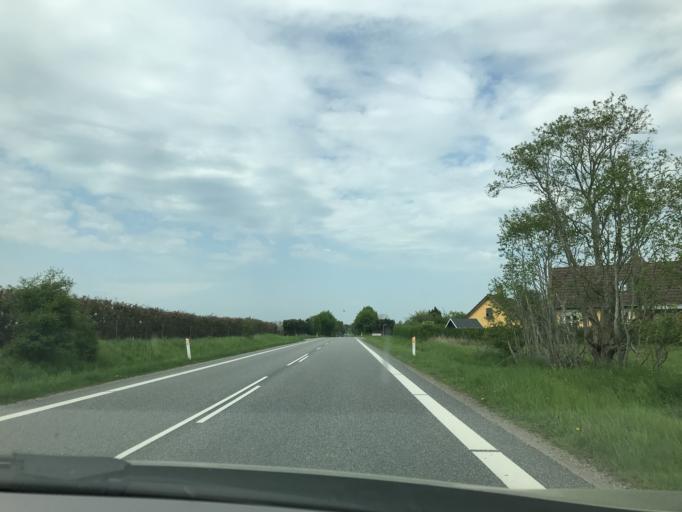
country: DK
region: South Denmark
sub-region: Assens Kommune
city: Assens
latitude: 55.3157
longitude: 9.9398
